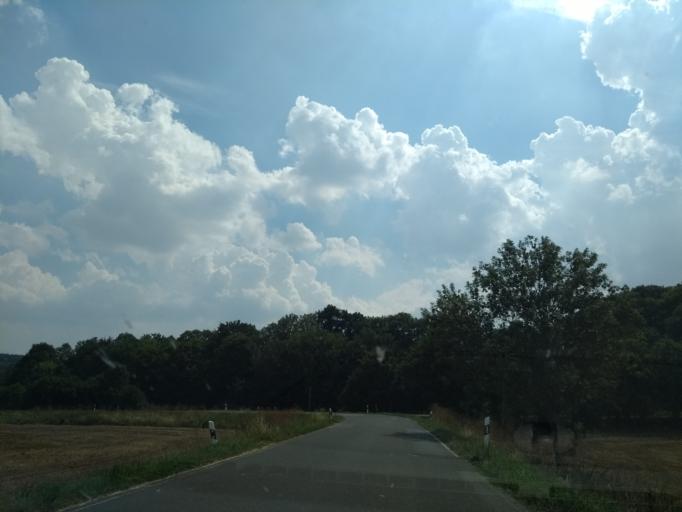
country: DE
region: Saxony-Anhalt
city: Kretzschau
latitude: 51.0238
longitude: 12.0774
